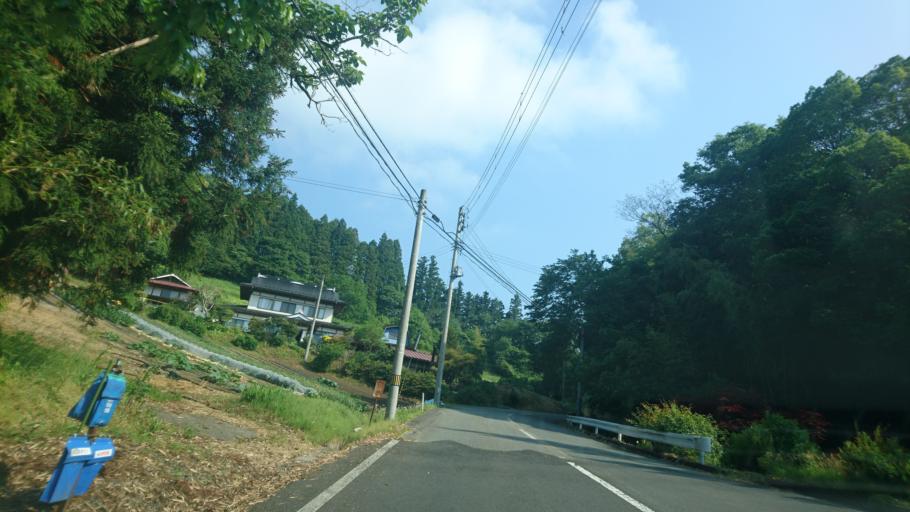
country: JP
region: Iwate
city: Ichinoseki
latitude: 38.9226
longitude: 141.2778
